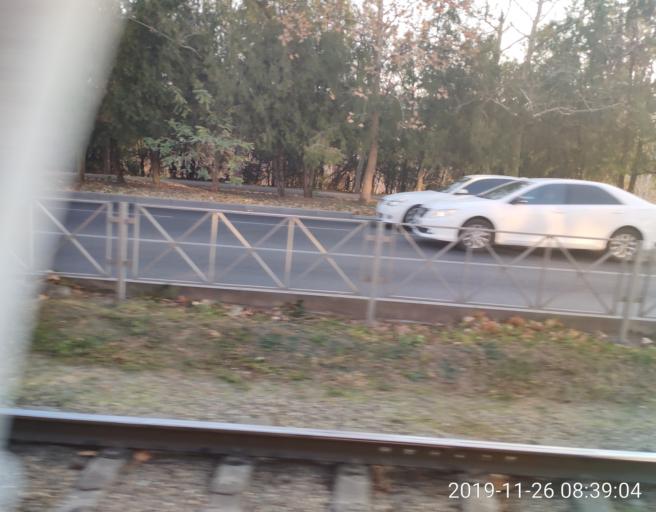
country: RU
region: Krasnodarskiy
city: Krasnodar
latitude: 45.0585
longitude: 38.9848
